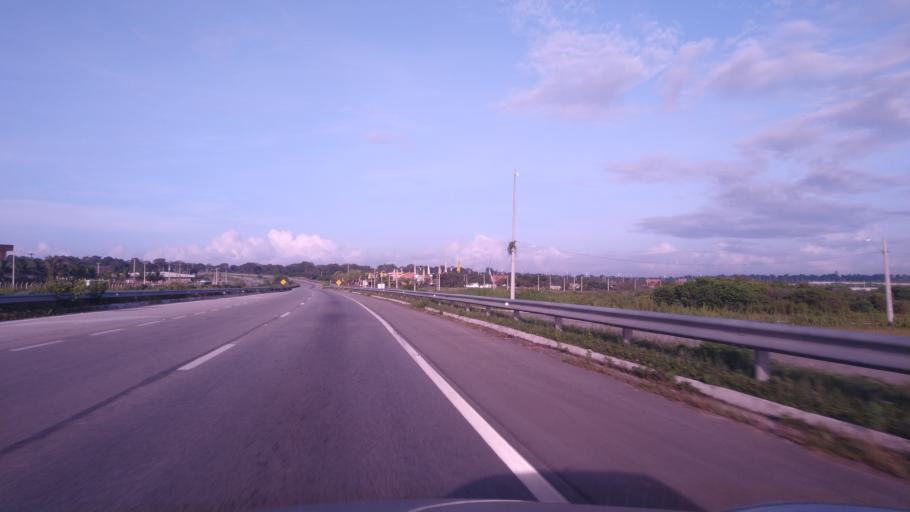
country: BR
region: Ceara
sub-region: Pacajus
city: Pacajus
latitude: -4.1645
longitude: -38.4889
